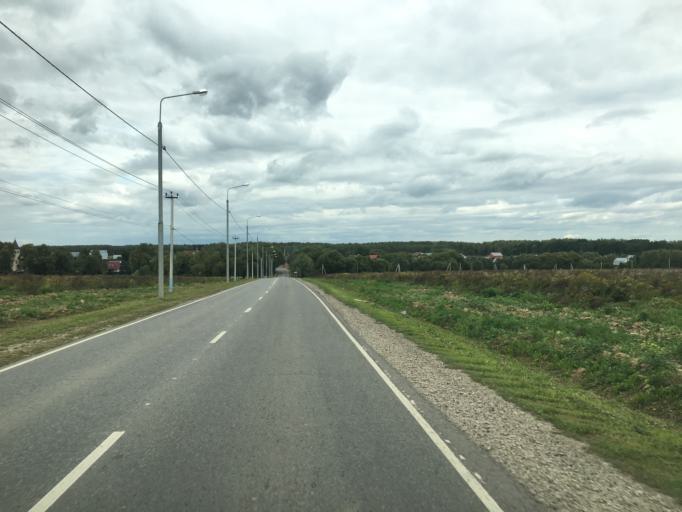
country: RU
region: Moskovskaya
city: Vatutinki
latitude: 55.4863
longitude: 37.4011
